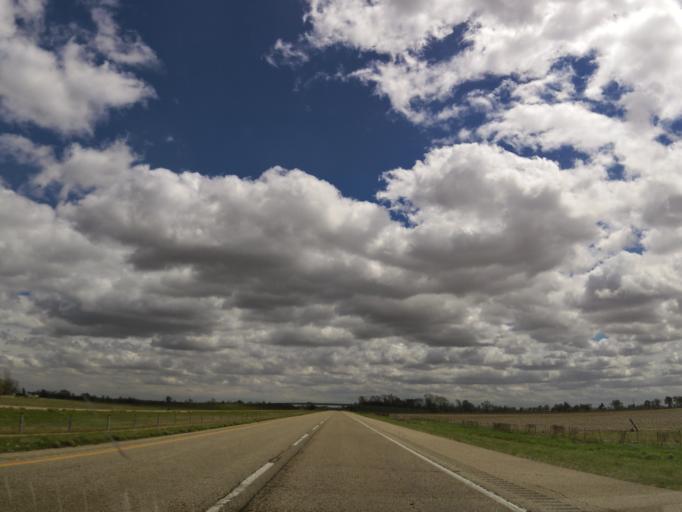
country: US
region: Arkansas
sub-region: Poinsett County
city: Trumann
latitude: 35.6571
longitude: -90.5420
